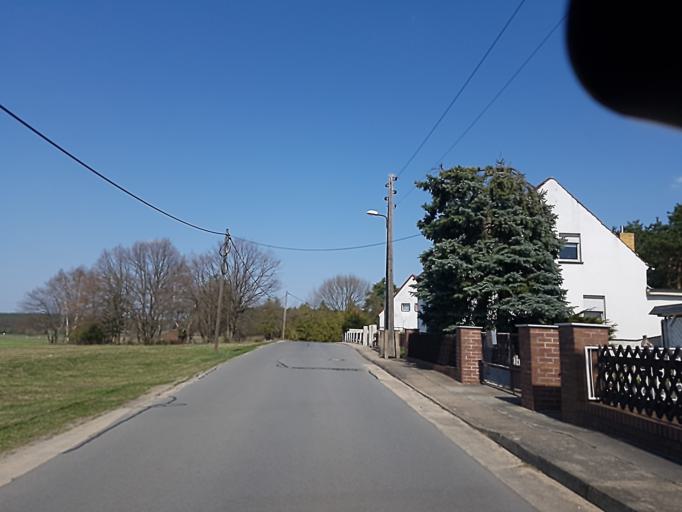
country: DE
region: Brandenburg
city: Bad Liebenwerda
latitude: 51.5402
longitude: 13.4469
